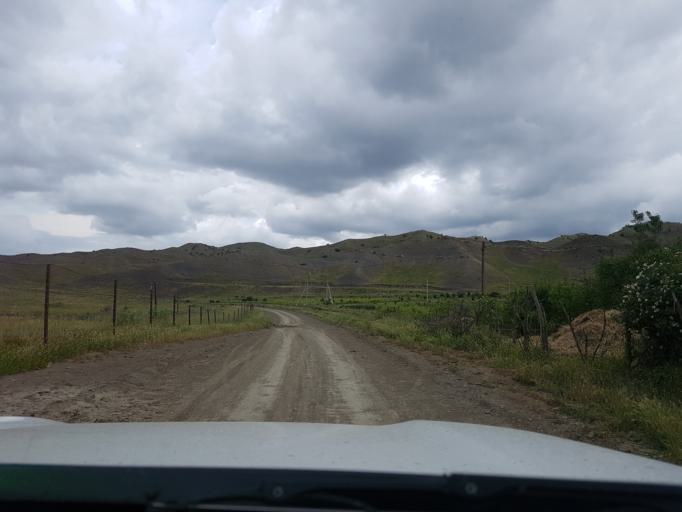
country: TM
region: Ahal
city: Baharly
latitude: 38.2152
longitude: 56.9944
